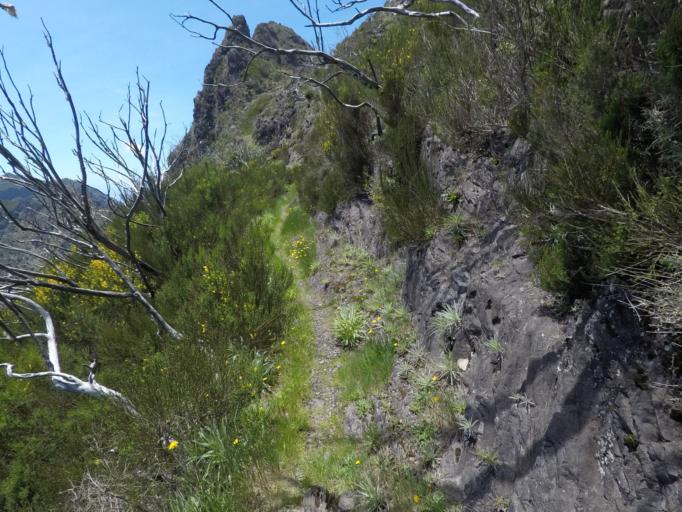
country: PT
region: Madeira
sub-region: Camara de Lobos
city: Curral das Freiras
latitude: 32.7552
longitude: -16.9752
